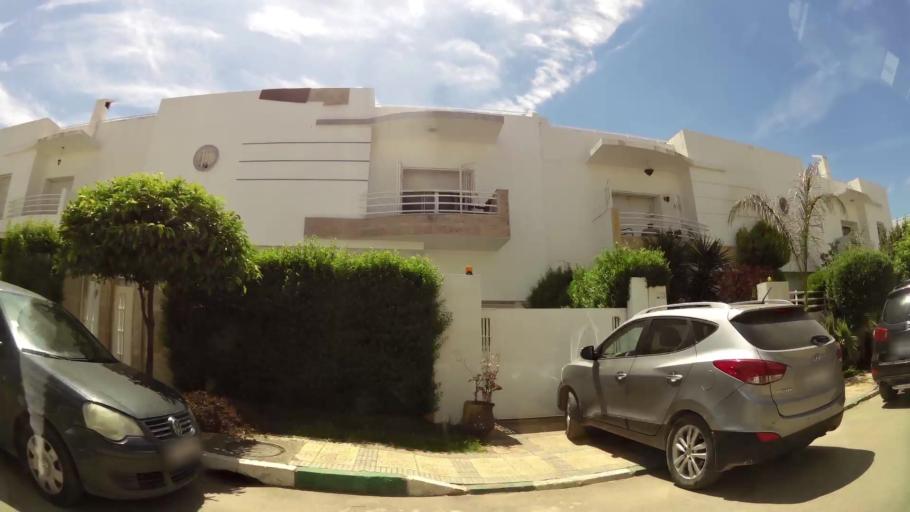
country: MA
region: Fes-Boulemane
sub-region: Fes
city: Fes
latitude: 34.0087
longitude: -4.9913
